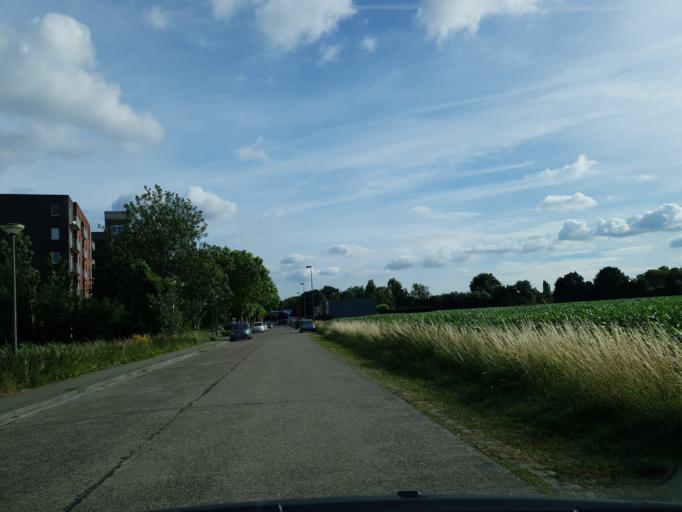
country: BE
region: Flanders
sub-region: Provincie Antwerpen
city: Brasschaat
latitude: 51.2610
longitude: 4.4504
